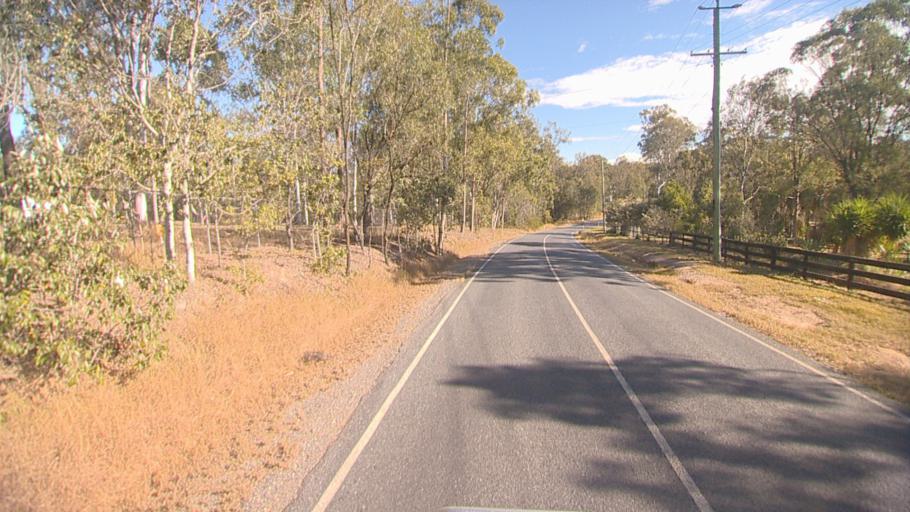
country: AU
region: Queensland
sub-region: Logan
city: Cedar Vale
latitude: -27.8354
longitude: 153.0506
